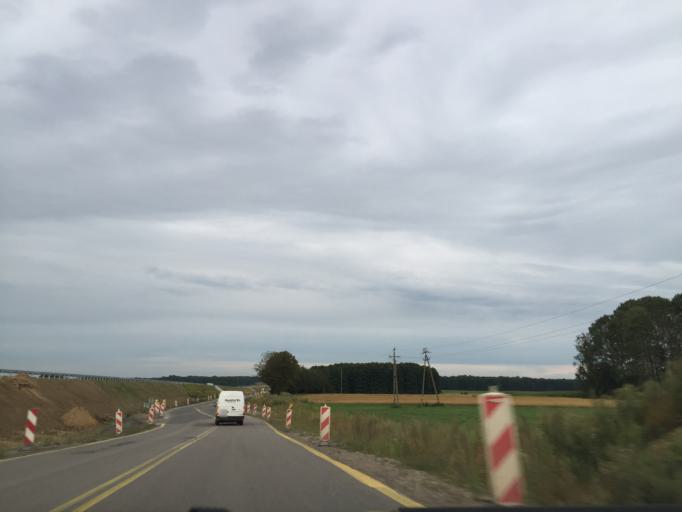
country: PL
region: Podlasie
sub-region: Powiat wysokomazowiecki
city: Sokoly
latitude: 53.1194
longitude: 22.6463
